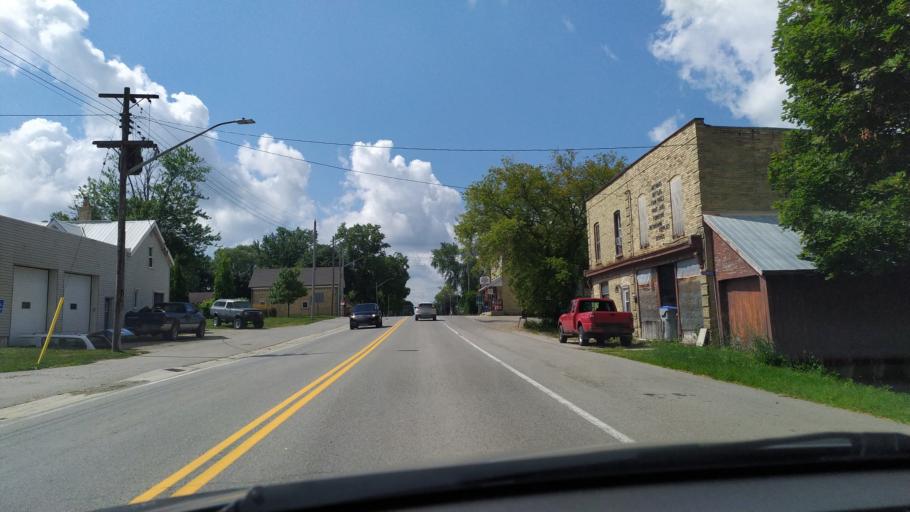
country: CA
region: Ontario
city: South Huron
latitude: 43.3250
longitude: -81.3128
